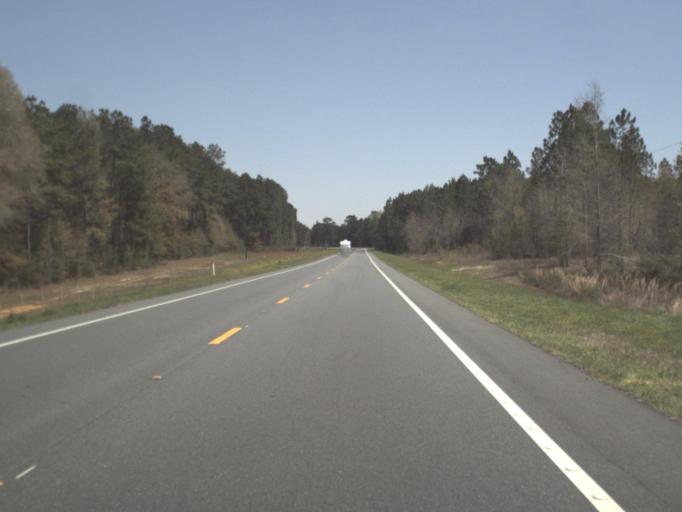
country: US
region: Florida
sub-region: Calhoun County
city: Blountstown
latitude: 30.4335
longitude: -85.2370
